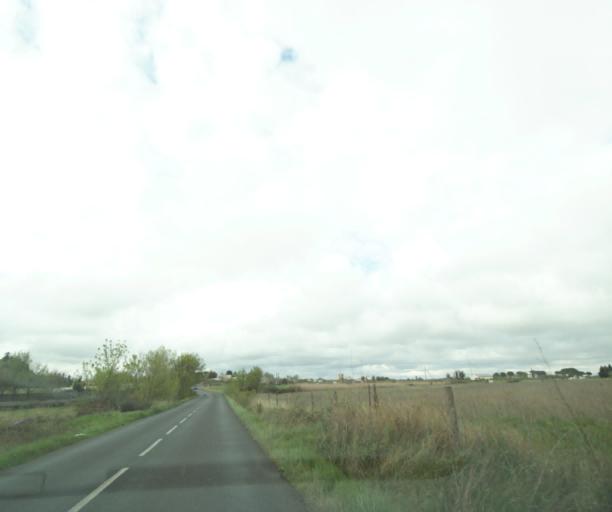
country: FR
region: Languedoc-Roussillon
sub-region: Departement de l'Herault
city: Saussan
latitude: 43.5615
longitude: 3.7757
